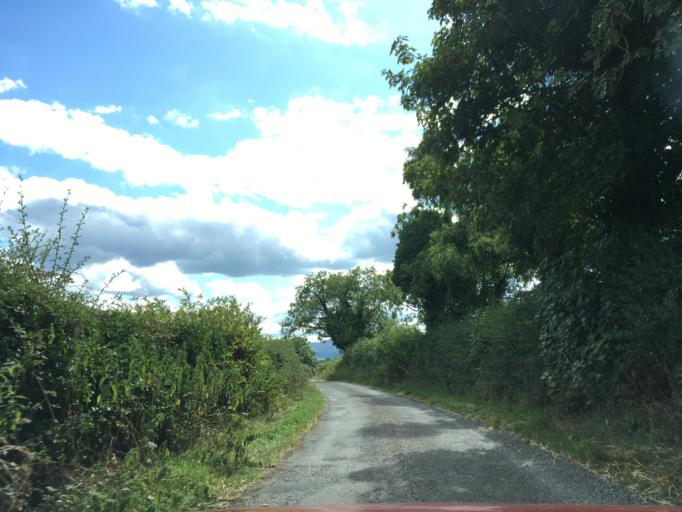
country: IE
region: Munster
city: Cashel
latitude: 52.4848
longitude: -7.9652
